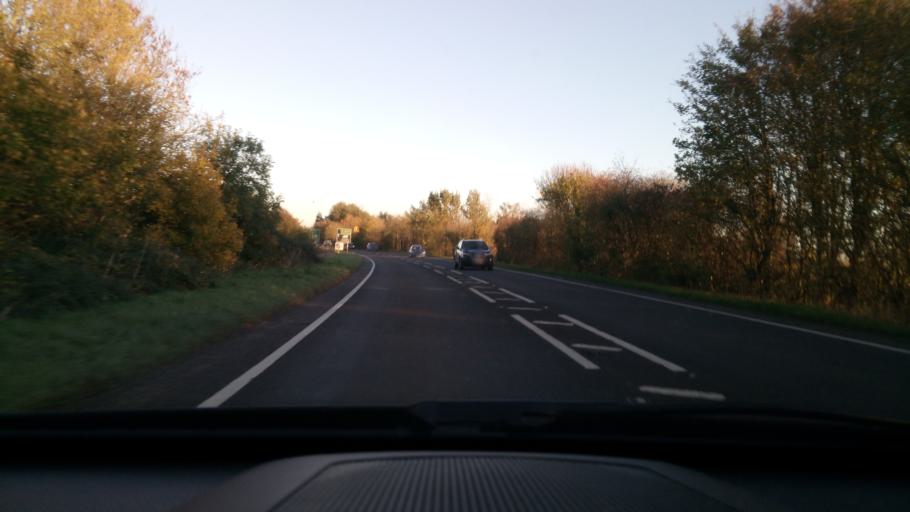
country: GB
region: England
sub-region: Peterborough
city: Glinton
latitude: 52.6325
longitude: -0.3010
